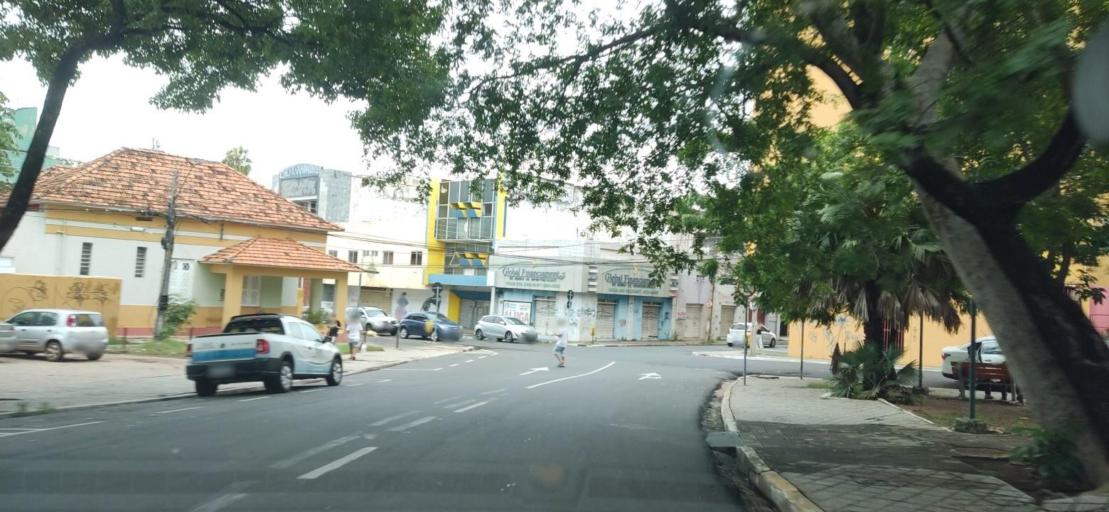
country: BR
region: Piaui
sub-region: Teresina
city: Teresina
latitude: -5.0899
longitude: -42.8116
